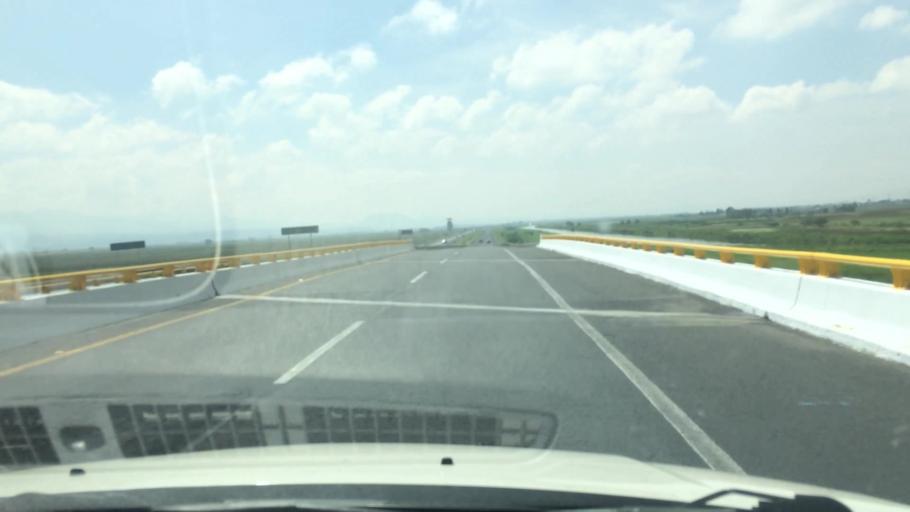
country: MX
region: Mexico
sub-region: Toluca
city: La Constitucion Toltepec
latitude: 19.3615
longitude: -99.5372
